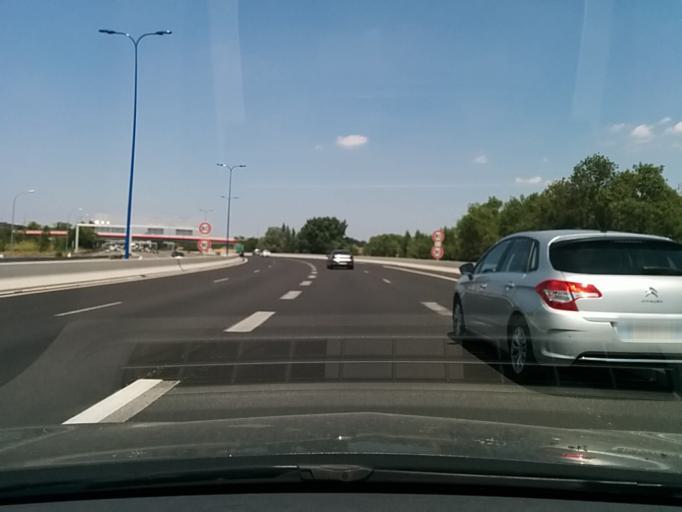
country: FR
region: Midi-Pyrenees
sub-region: Departement de la Haute-Garonne
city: Ramonville-Saint-Agne
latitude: 43.5611
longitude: 1.4892
